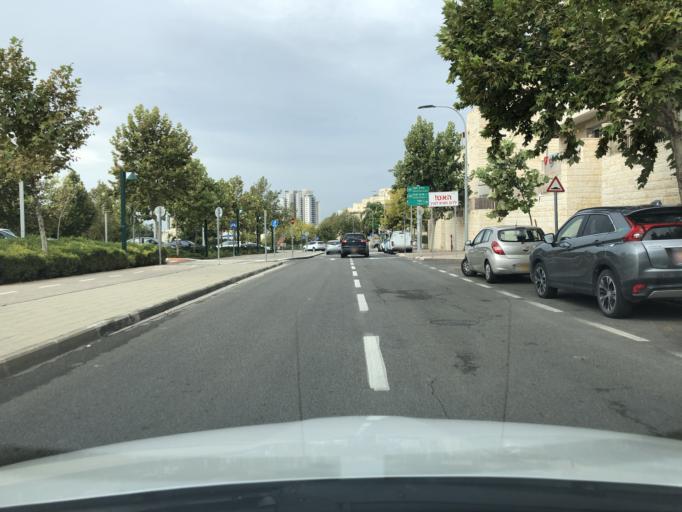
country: IL
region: Central District
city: Modiin
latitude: 31.9127
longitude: 35.0111
